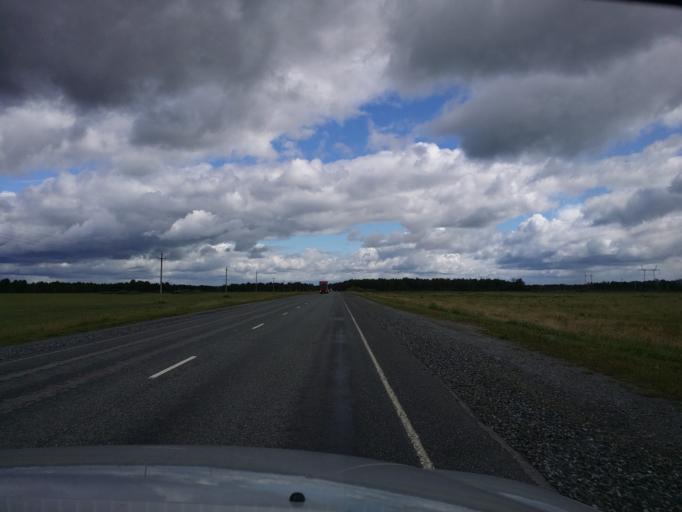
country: RU
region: Tjumen
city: Sumkino
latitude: 57.8667
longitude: 68.0623
